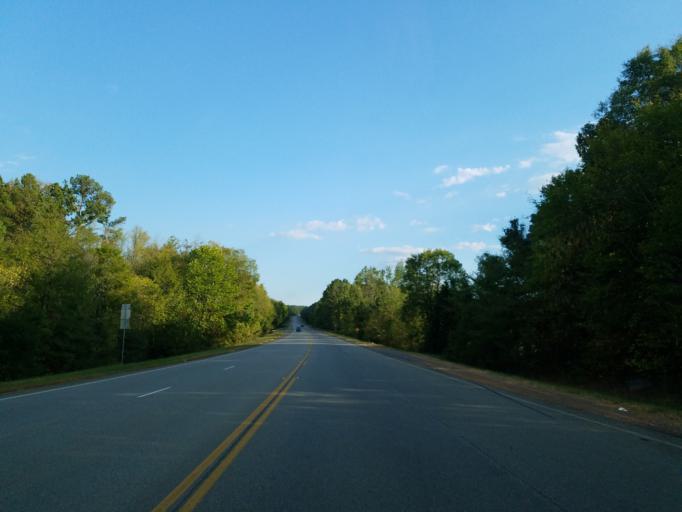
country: US
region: Georgia
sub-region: Murray County
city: Chatsworth
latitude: 34.6950
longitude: -84.7370
